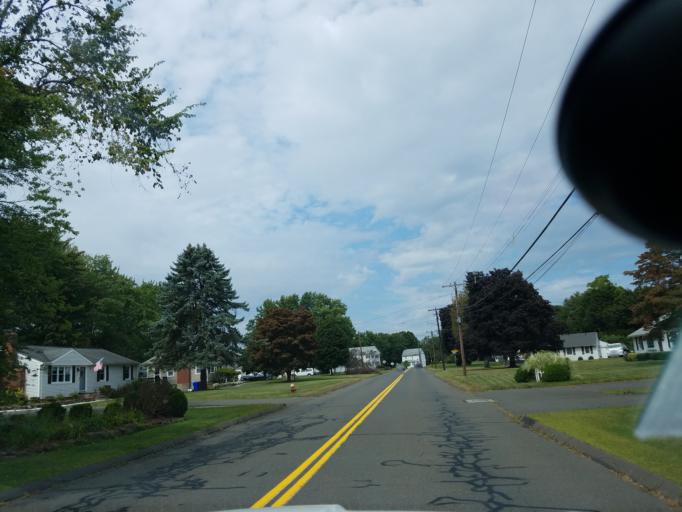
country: US
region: Connecticut
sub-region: Hartford County
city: Wethersfield
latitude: 41.6617
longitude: -72.6458
